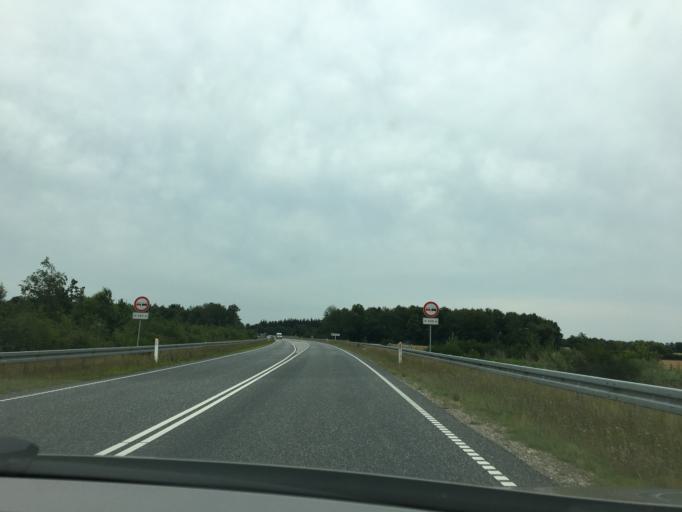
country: DK
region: Central Jutland
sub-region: Herning Kommune
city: Sunds
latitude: 56.2052
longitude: 8.9902
